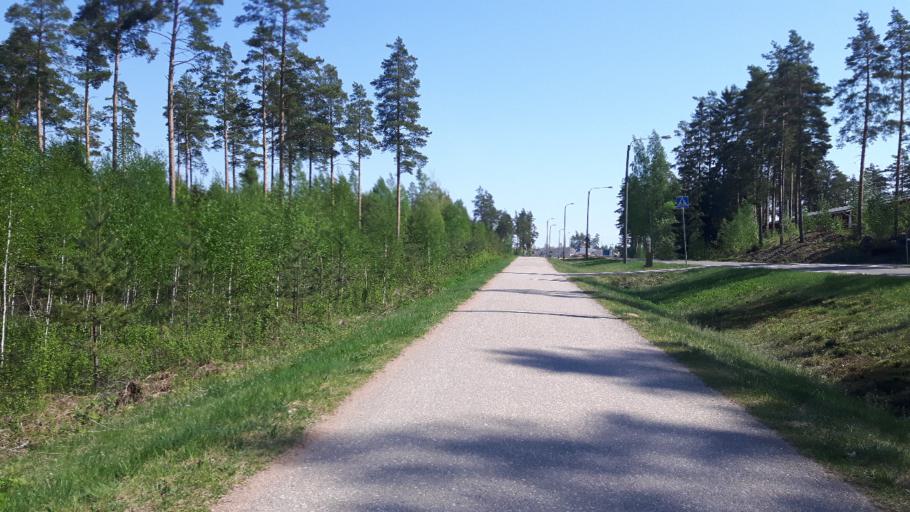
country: FI
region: Kymenlaakso
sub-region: Kotka-Hamina
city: Pyhtaeae
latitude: 60.4907
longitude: 26.5563
